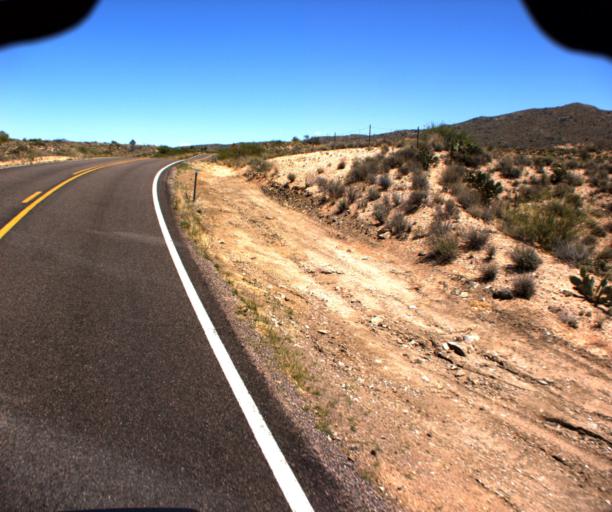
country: US
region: Arizona
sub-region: Yavapai County
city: Bagdad
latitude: 34.4992
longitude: -113.1729
